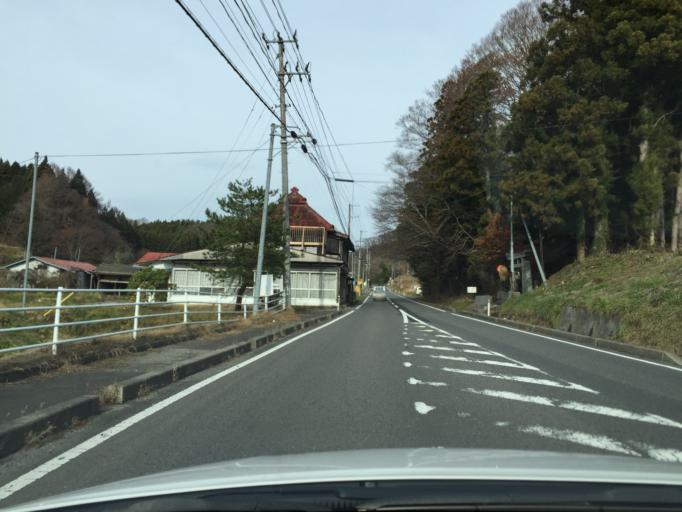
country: JP
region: Fukushima
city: Funehikimachi-funehiki
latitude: 37.3699
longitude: 140.6007
